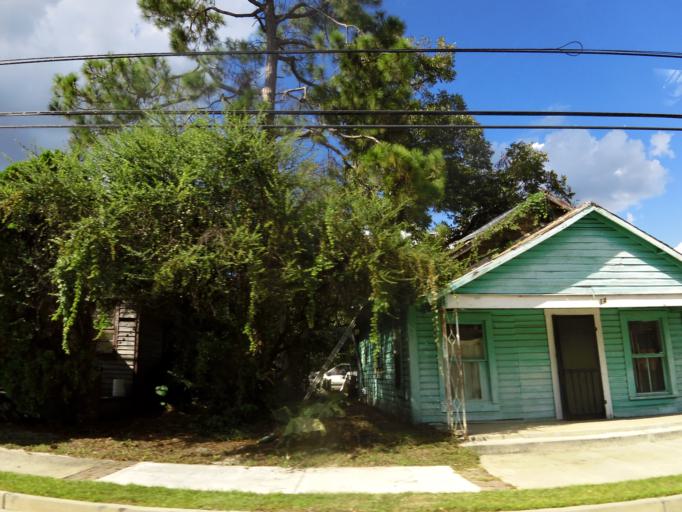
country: US
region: Georgia
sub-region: Lowndes County
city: Valdosta
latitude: 30.8272
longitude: -83.2746
